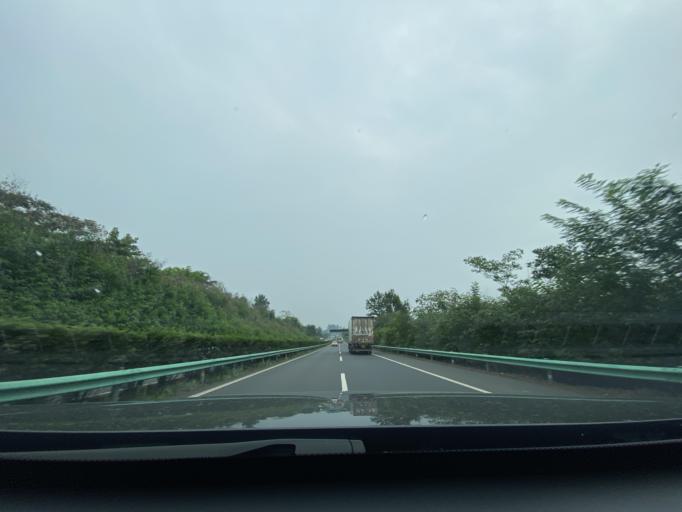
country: CN
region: Sichuan
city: Longquan
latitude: 30.3125
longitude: 104.1191
